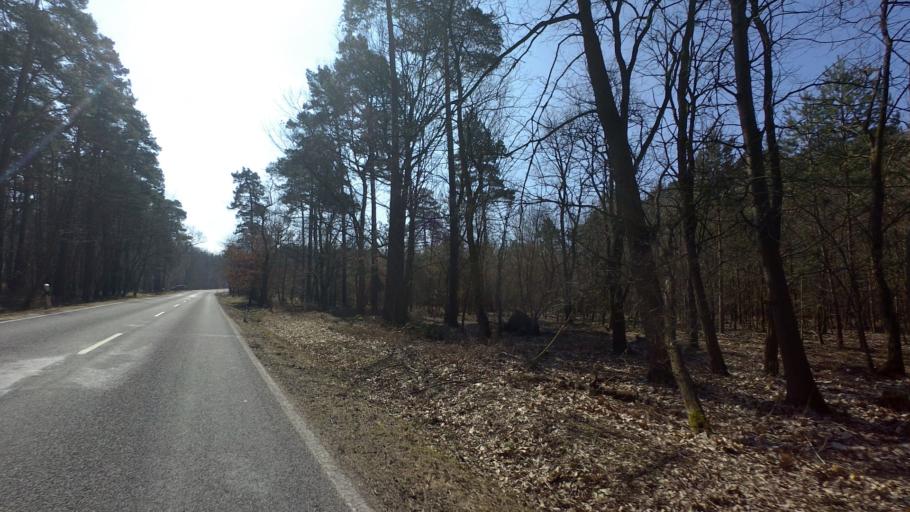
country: DE
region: Saxony-Anhalt
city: Nudersdorf
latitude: 51.9722
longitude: 12.5873
